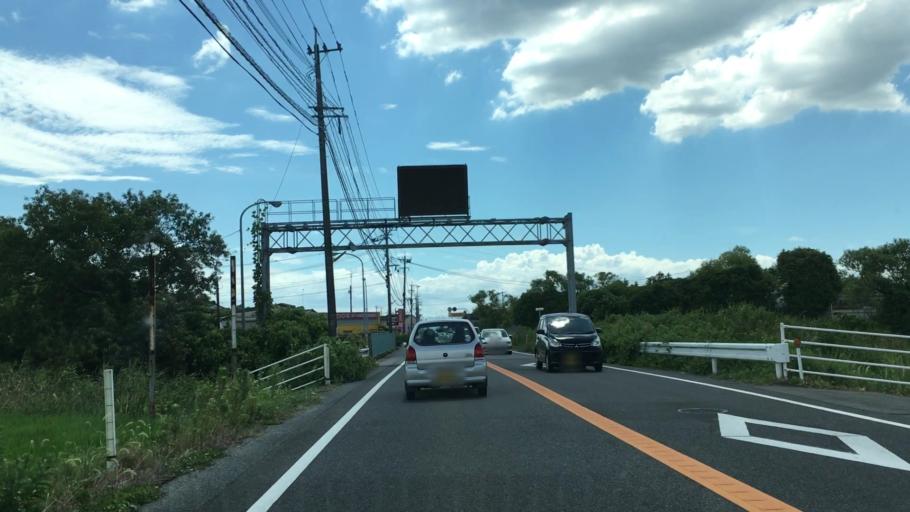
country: JP
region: Saga Prefecture
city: Kanzakimachi-kanzaki
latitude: 33.2896
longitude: 130.3529
